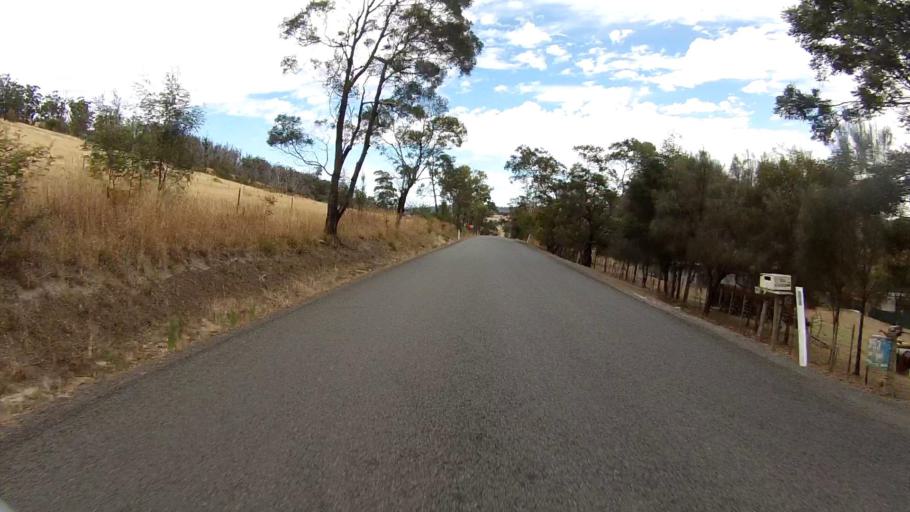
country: AU
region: Tasmania
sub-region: Sorell
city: Sorell
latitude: -42.8778
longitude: 147.7070
